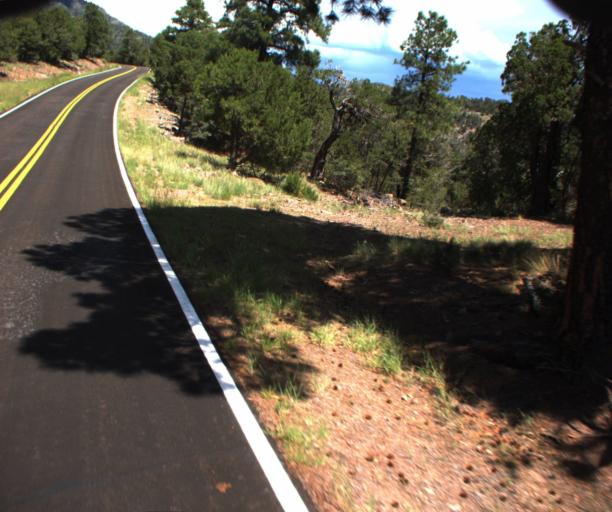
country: US
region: Arizona
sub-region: Greenlee County
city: Morenci
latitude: 33.4053
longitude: -109.3486
